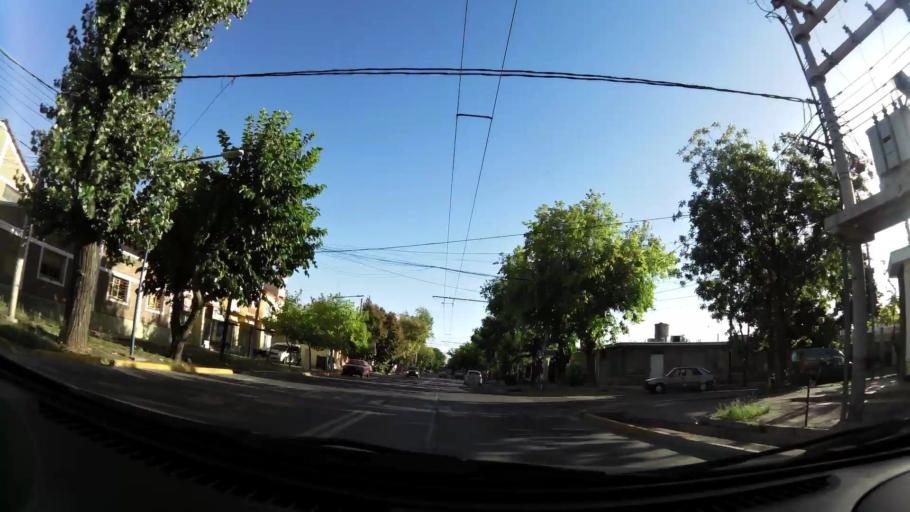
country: AR
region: Mendoza
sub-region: Departamento de Godoy Cruz
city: Godoy Cruz
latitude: -32.9436
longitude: -68.8487
